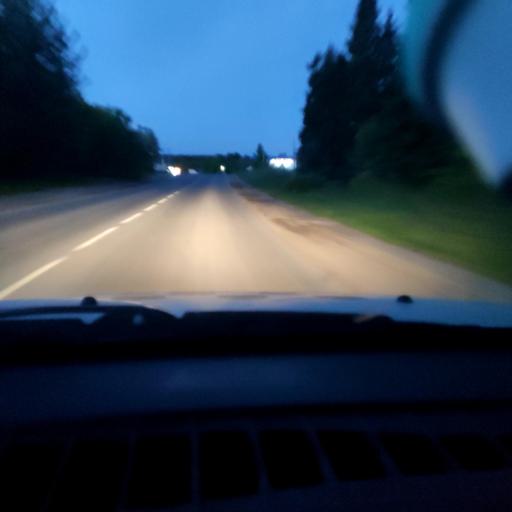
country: RU
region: Perm
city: Polazna
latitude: 58.2902
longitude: 56.4050
